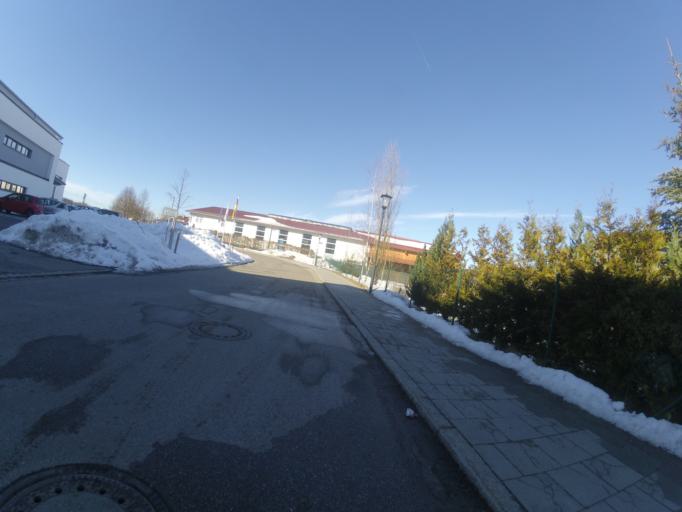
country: DE
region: Bavaria
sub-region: Upper Bavaria
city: Aying
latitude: 47.9707
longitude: 11.7678
